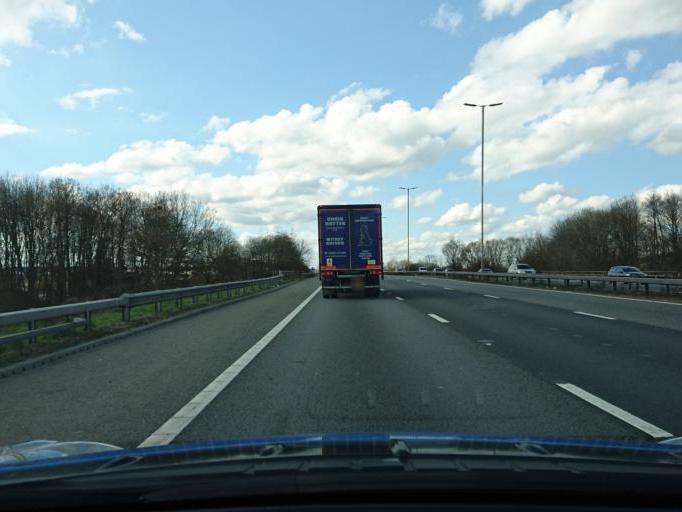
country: GB
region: England
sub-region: West Berkshire
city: Calcot
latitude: 51.4339
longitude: -1.0540
